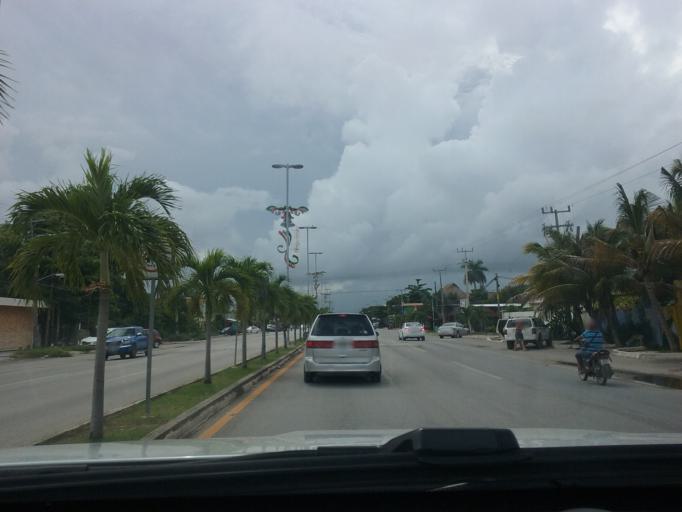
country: MX
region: Quintana Roo
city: Tulum
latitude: 20.2092
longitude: -87.4692
